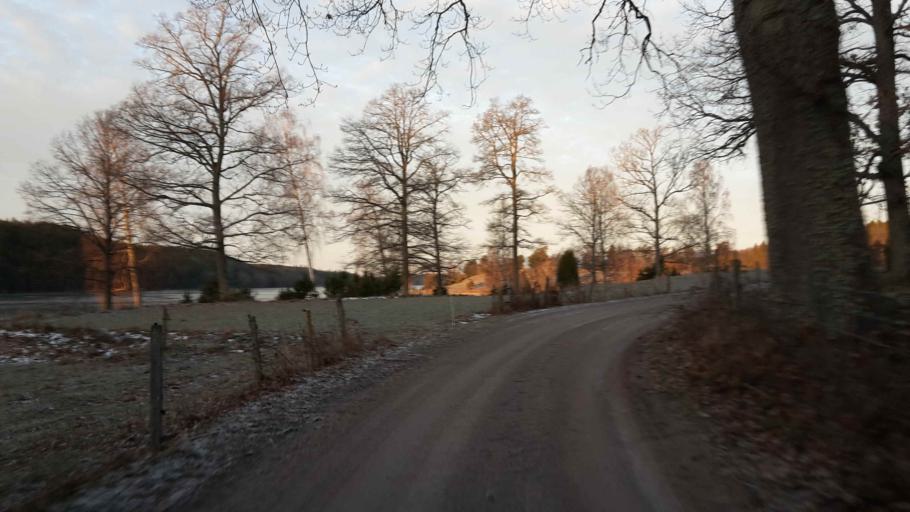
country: SE
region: OEstergoetland
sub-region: Atvidabergs Kommun
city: Atvidaberg
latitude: 58.2726
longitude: 16.1190
